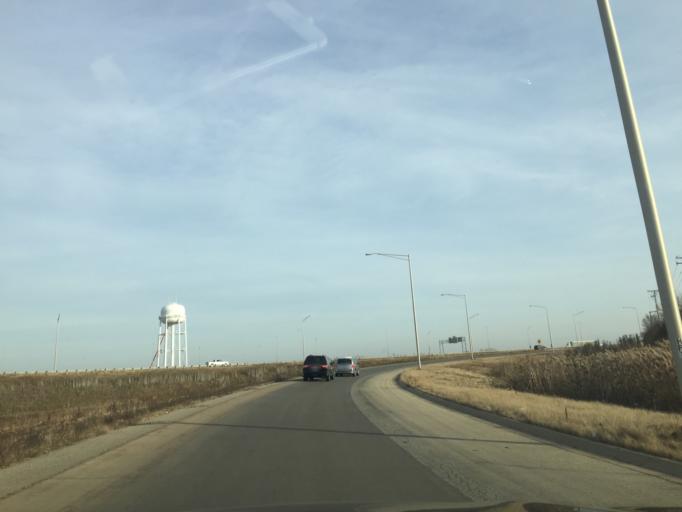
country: US
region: Illinois
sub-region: Will County
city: Bolingbrook
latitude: 41.7013
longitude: -88.0340
